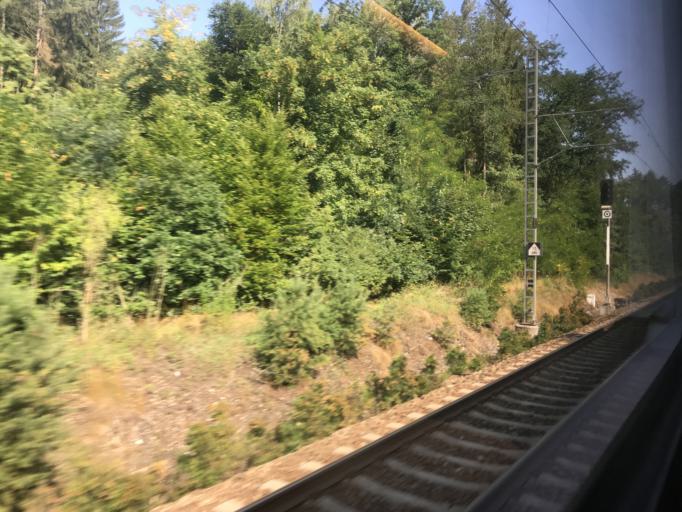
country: CZ
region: Central Bohemia
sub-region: Okres Benesov
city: Cercany
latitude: 49.8811
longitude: 14.7268
